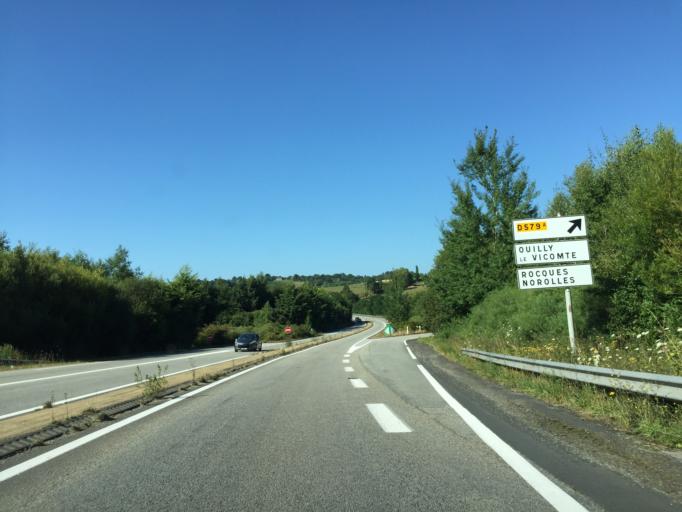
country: FR
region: Lower Normandy
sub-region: Departement du Calvados
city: Lisieux
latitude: 49.1769
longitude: 0.2262
